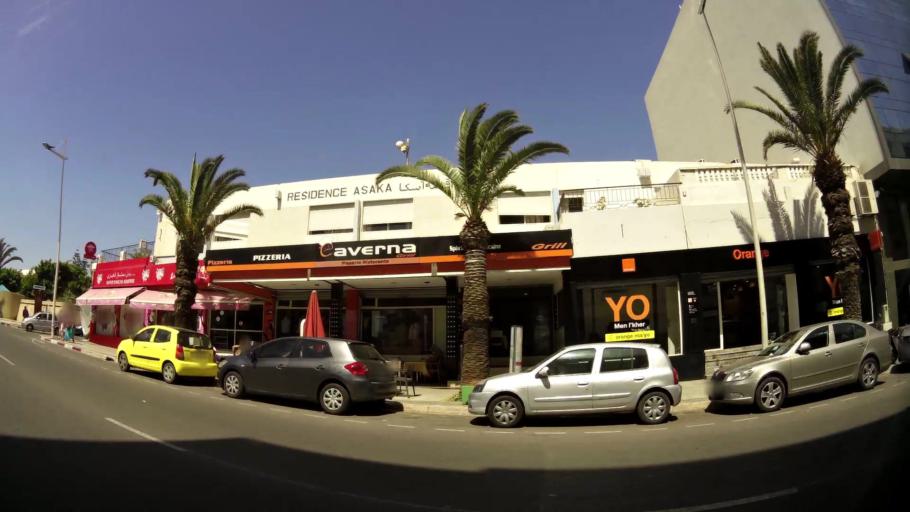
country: MA
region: Souss-Massa-Draa
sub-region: Agadir-Ida-ou-Tnan
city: Agadir
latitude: 30.4189
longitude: -9.5979
